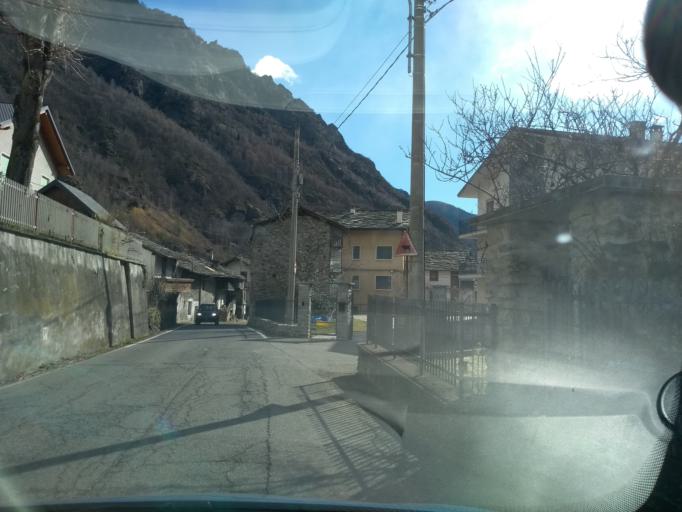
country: IT
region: Piedmont
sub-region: Provincia di Torino
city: Chialamberto
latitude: 45.3581
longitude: 7.3549
